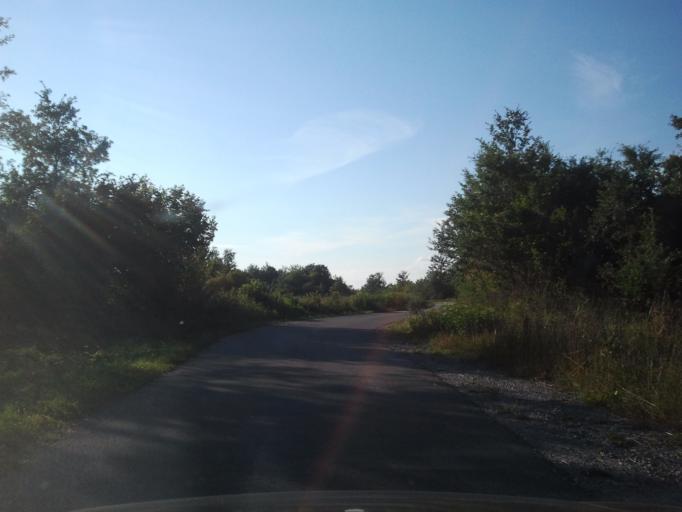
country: HR
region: Zadarska
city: Gracac
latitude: 44.3832
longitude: 15.6997
